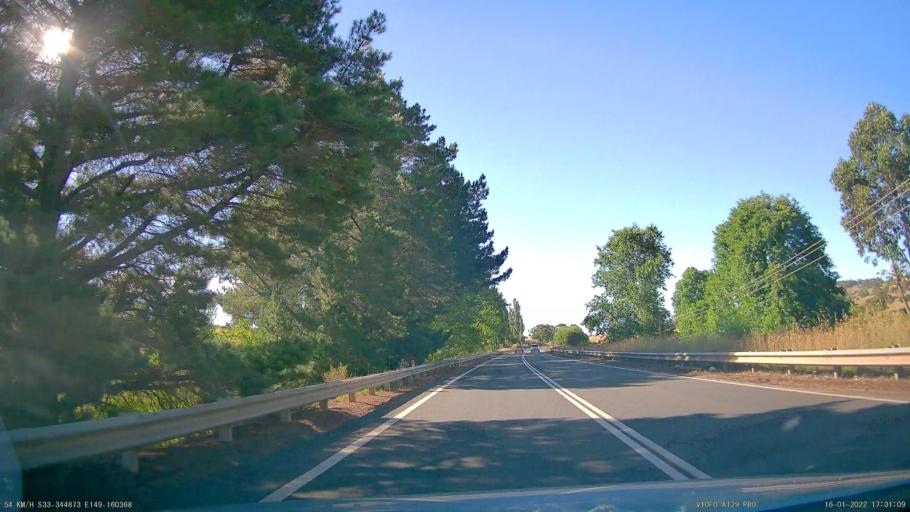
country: AU
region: New South Wales
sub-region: Orange Municipality
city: Orange
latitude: -33.3448
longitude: 149.1603
